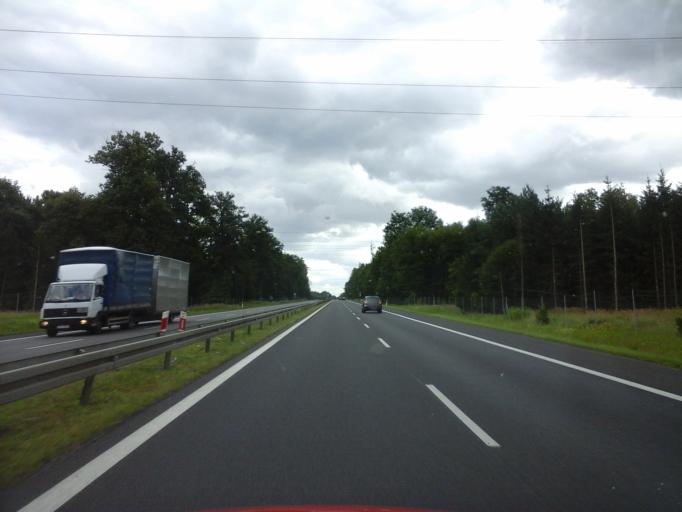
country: PL
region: West Pomeranian Voivodeship
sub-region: Powiat stargardzki
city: Kobylanka
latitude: 53.3550
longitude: 14.7981
